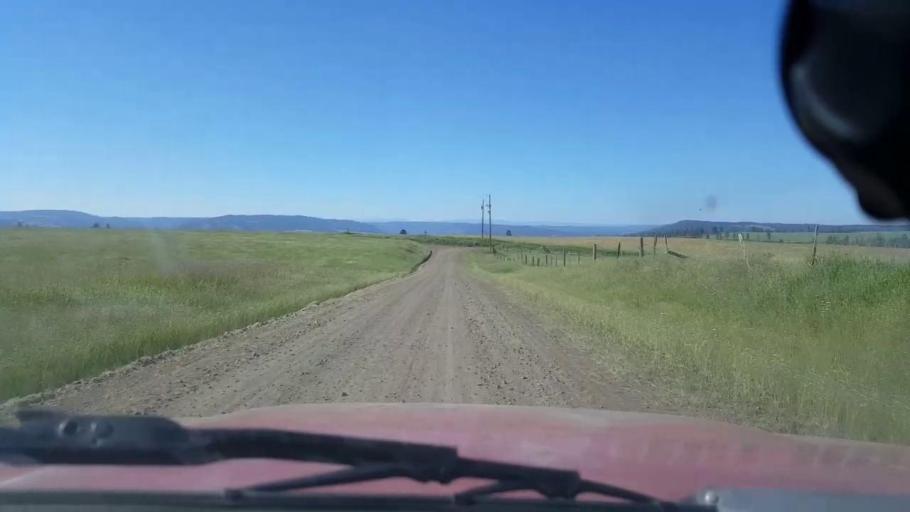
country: US
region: Washington
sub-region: Garfield County
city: Pomeroy
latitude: 45.9859
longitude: -117.4580
